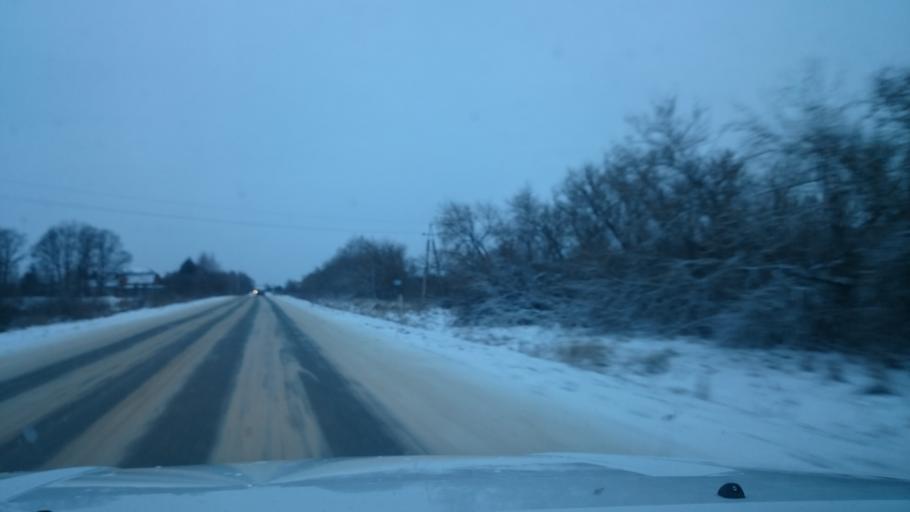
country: RU
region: Tula
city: Leninskiy
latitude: 54.2492
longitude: 37.3846
